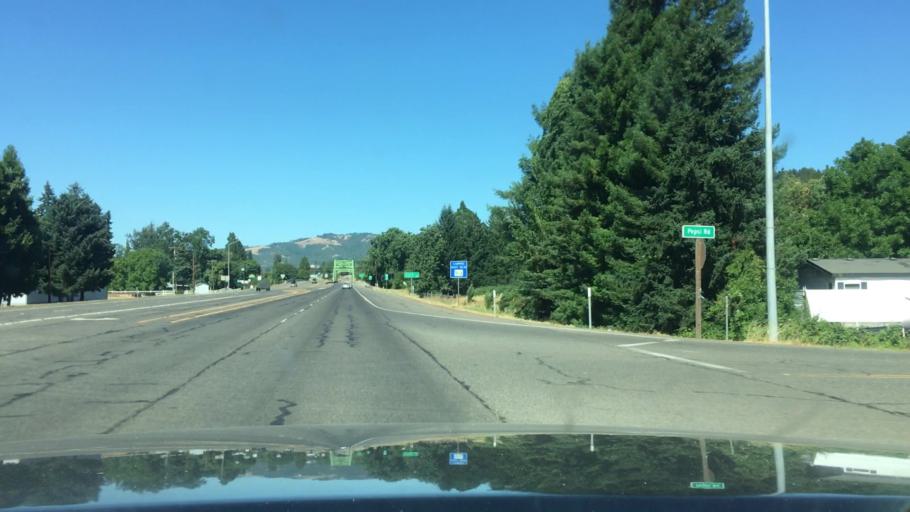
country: US
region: Oregon
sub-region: Douglas County
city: Winston
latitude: 43.1313
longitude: -123.4034
